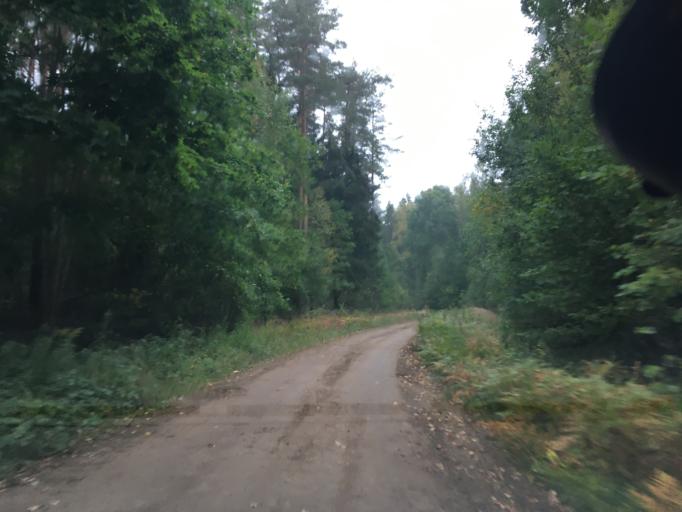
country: LV
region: Kuldigas Rajons
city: Kuldiga
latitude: 56.9868
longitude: 22.0122
